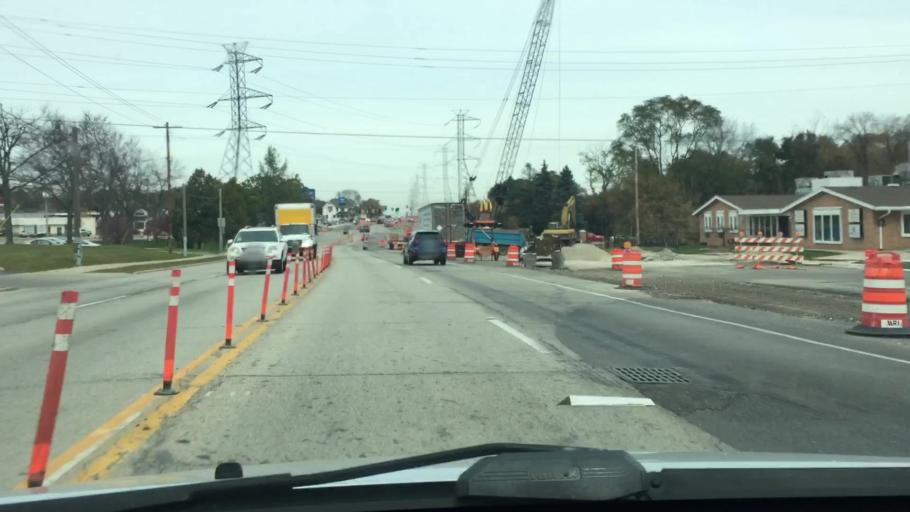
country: US
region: Wisconsin
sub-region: Milwaukee County
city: Hales Corners
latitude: 42.9336
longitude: -88.0485
